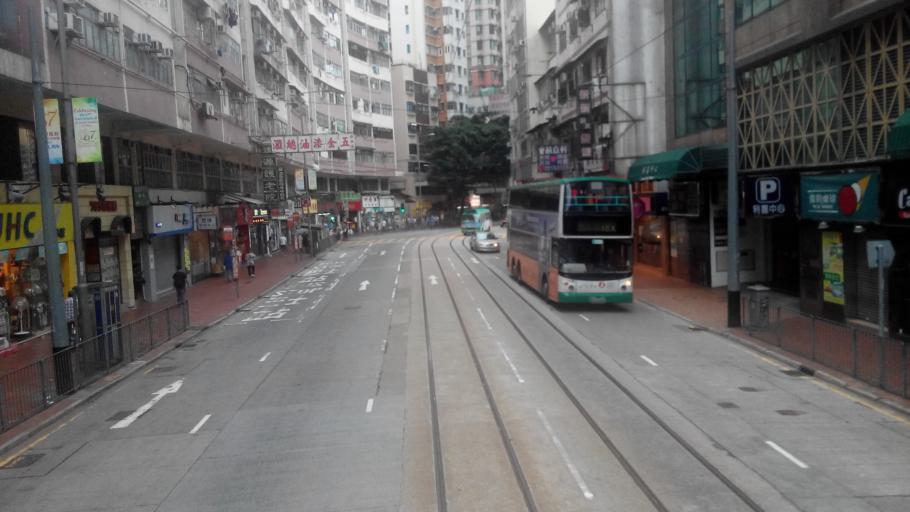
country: HK
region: Wanchai
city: Wan Chai
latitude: 22.2772
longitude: 114.2277
